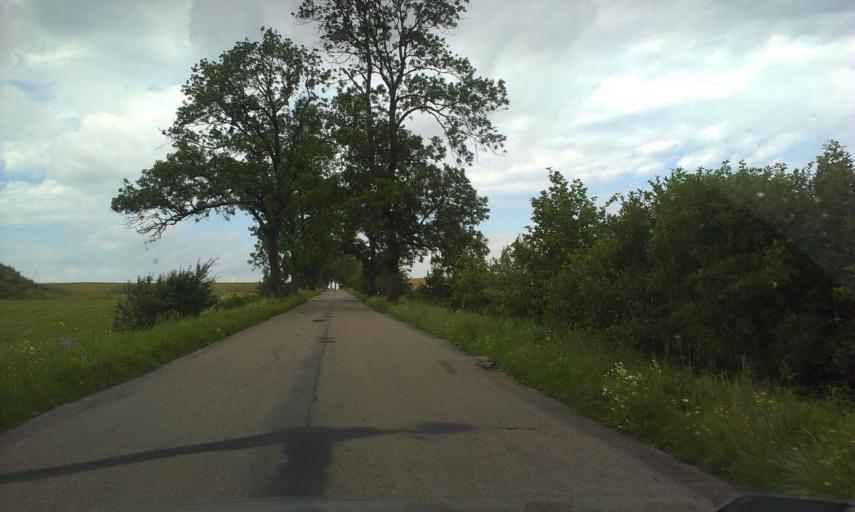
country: PL
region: West Pomeranian Voivodeship
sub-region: Powiat szczecinecki
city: Barwice
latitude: 53.7217
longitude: 16.3546
